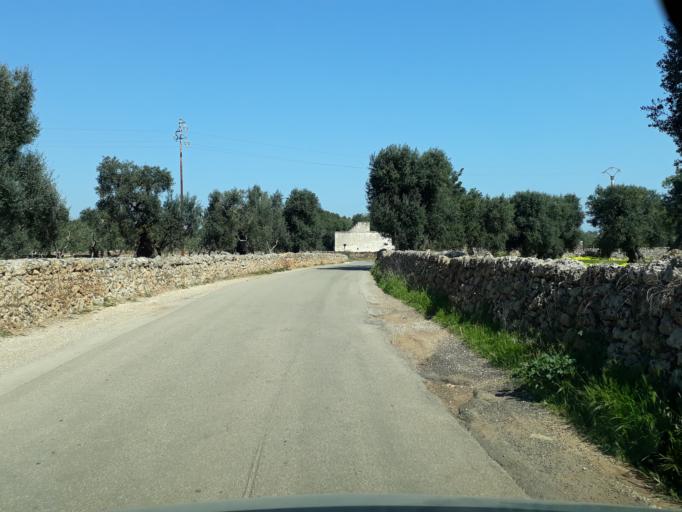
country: IT
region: Apulia
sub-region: Provincia di Brindisi
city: Fasano
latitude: 40.8341
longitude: 17.3784
